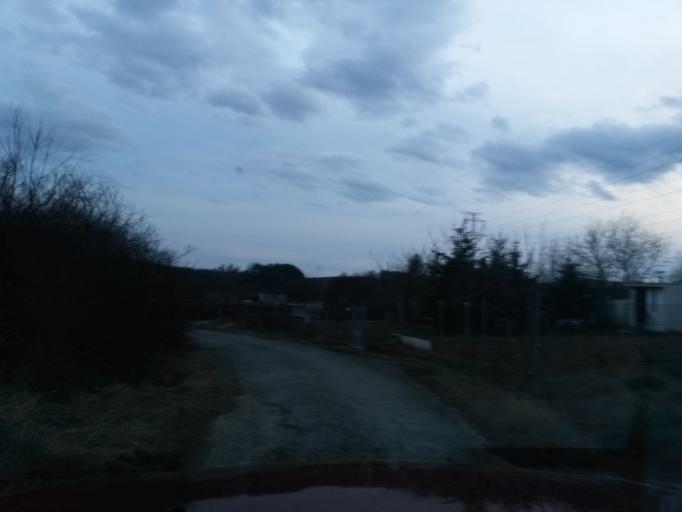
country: SK
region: Kosicky
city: Kosice
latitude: 48.7278
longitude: 21.3065
